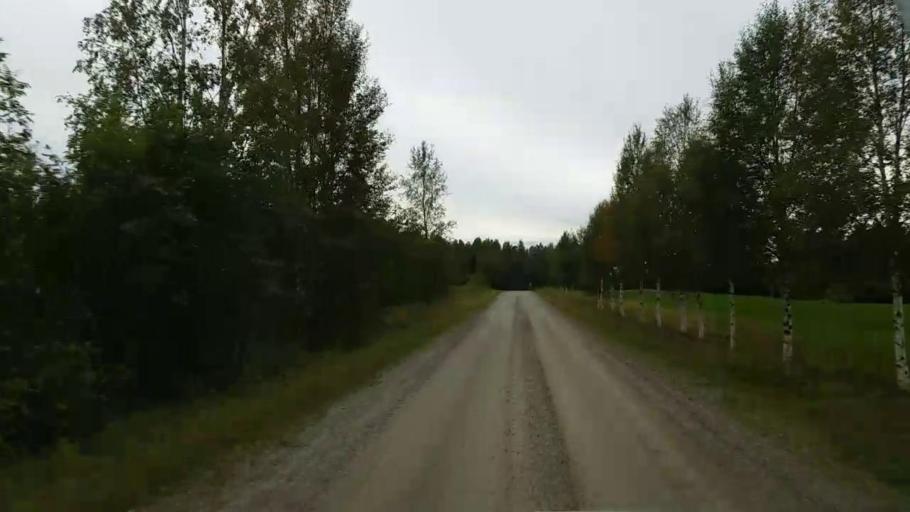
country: SE
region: Gaevleborg
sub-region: Ljusdals Kommun
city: Farila
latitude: 61.8083
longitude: 15.8617
